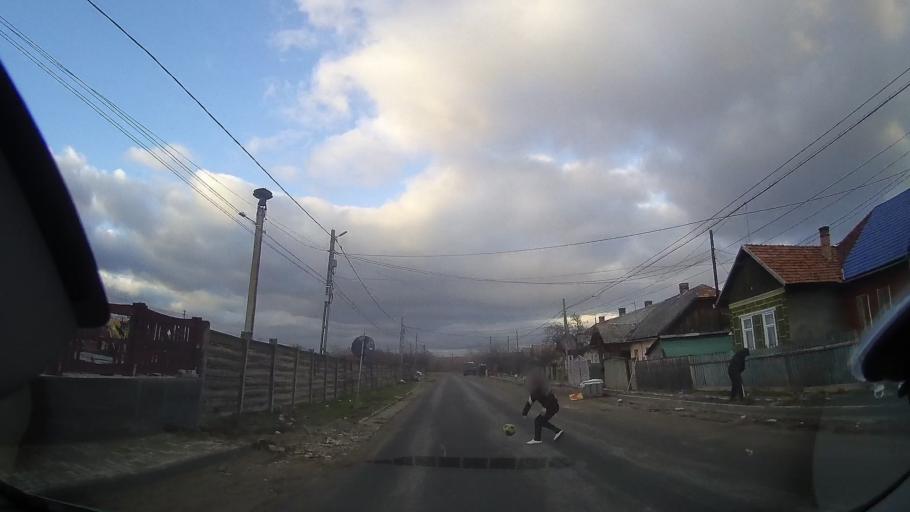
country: RO
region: Cluj
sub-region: Comuna Calatele
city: Calatele
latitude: 46.7684
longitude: 23.0084
